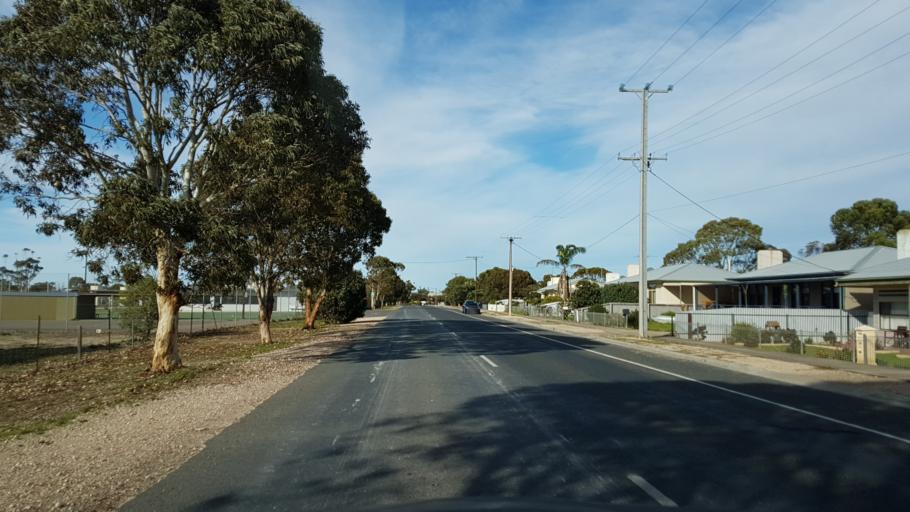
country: AU
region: South Australia
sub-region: Murray Bridge
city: Tailem Bend
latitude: -35.2470
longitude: 139.4550
